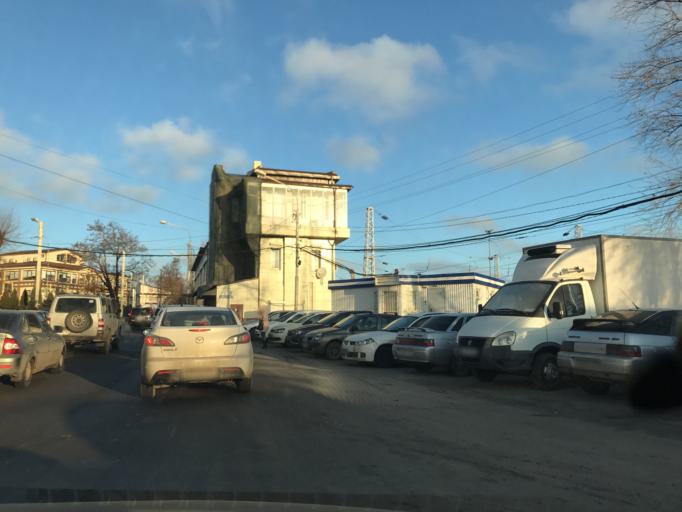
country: RU
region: Rostov
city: Rostov-na-Donu
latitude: 47.2202
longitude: 39.6864
